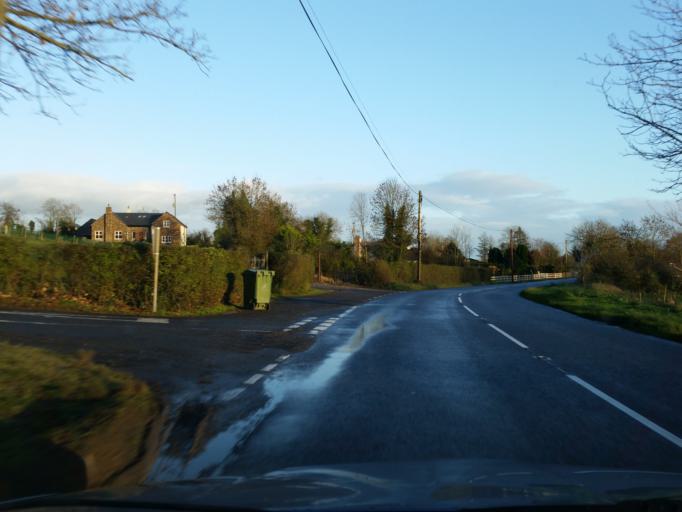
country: GB
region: Northern Ireland
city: Lisnaskea
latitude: 54.1963
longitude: -7.5255
